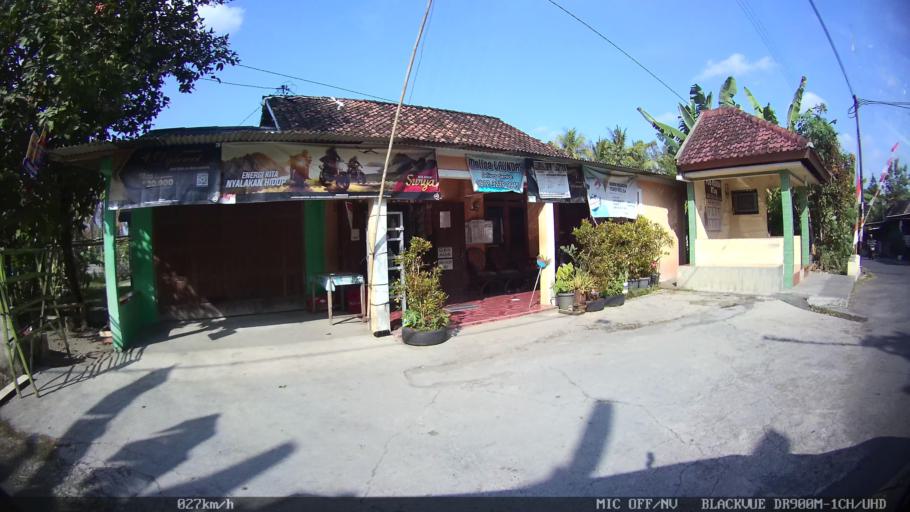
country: ID
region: Daerah Istimewa Yogyakarta
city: Kasihan
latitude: -7.8199
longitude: 110.2936
